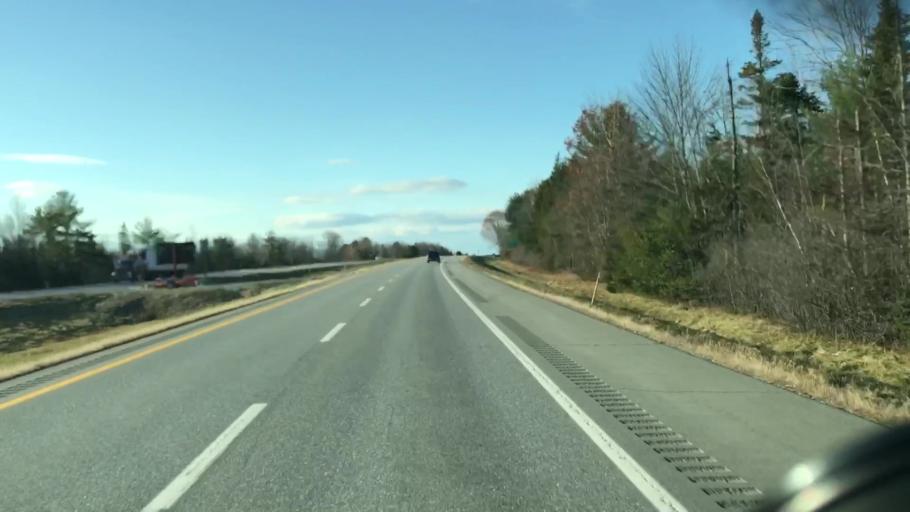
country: US
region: Maine
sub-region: Penobscot County
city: Newport
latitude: 44.8158
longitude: -69.2519
